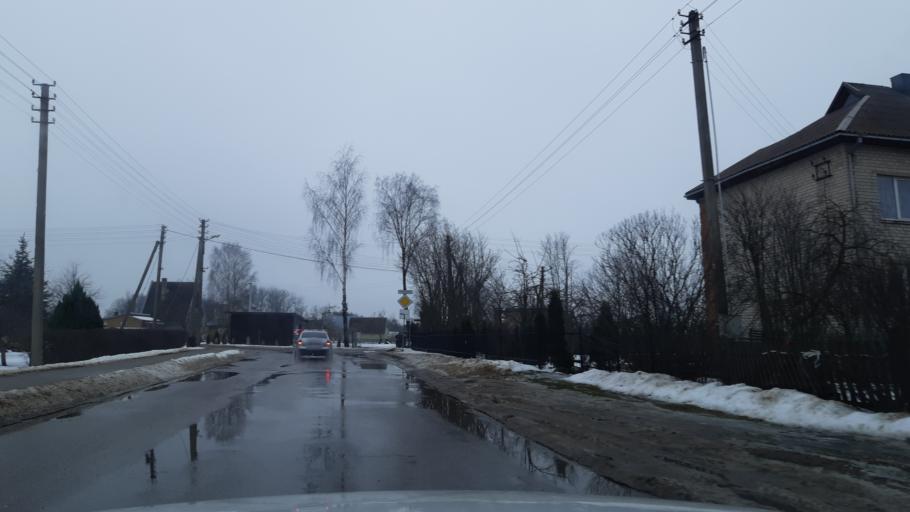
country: LT
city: Vilkaviskis
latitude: 54.6453
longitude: 23.0186
